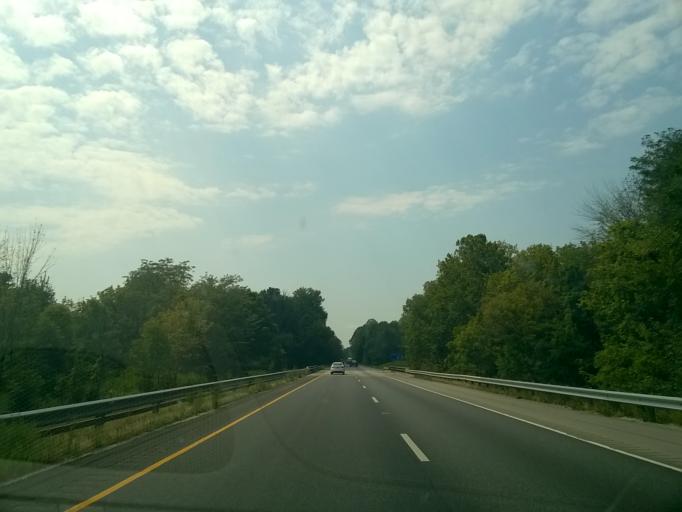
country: US
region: Indiana
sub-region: Clay County
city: Brazil
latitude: 39.4576
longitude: -87.0915
